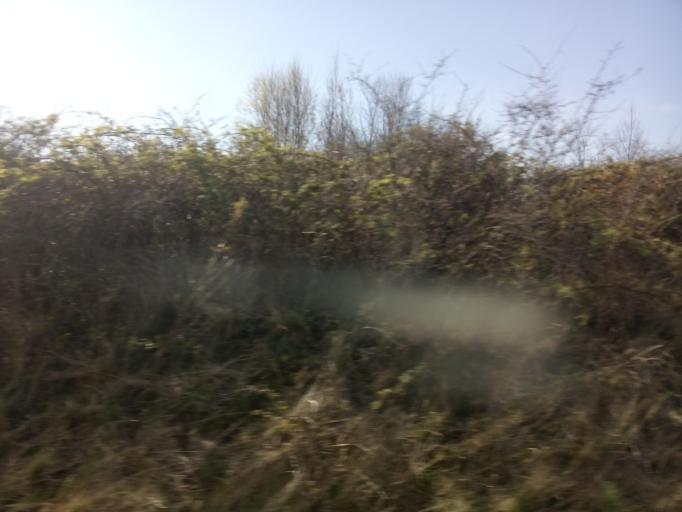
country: GB
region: Scotland
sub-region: East Lothian
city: Dunbar
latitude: 55.9892
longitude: -2.5704
